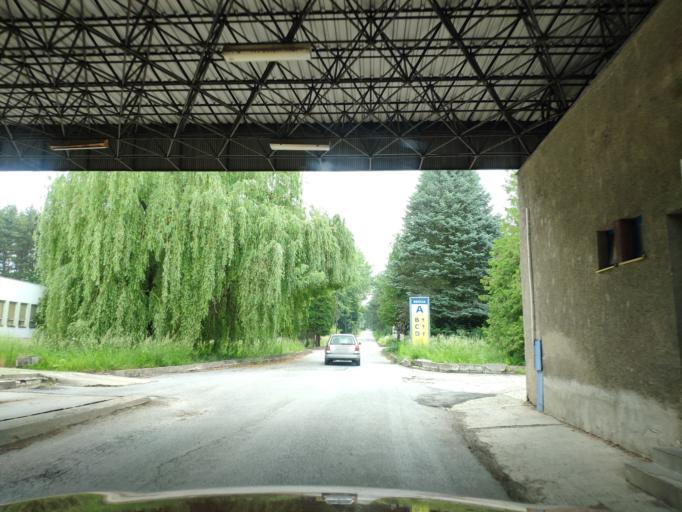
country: SK
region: Presovsky
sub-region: Okres Presov
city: Presov
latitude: 48.9995
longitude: 21.3107
